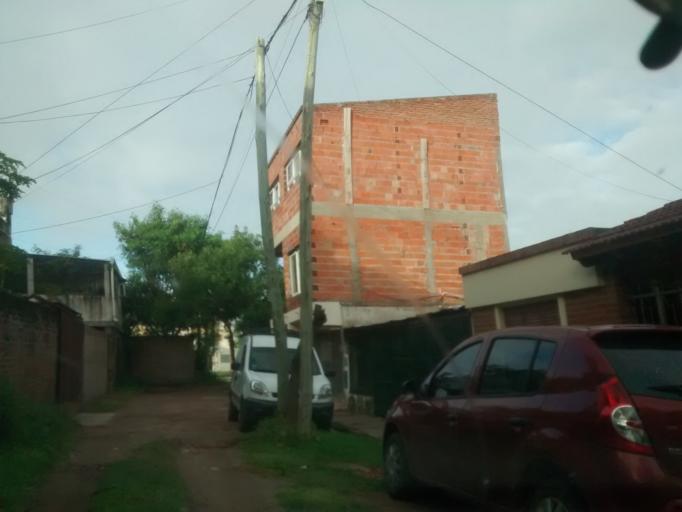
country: AR
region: Chaco
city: Fontana
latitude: -27.4477
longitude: -59.0132
